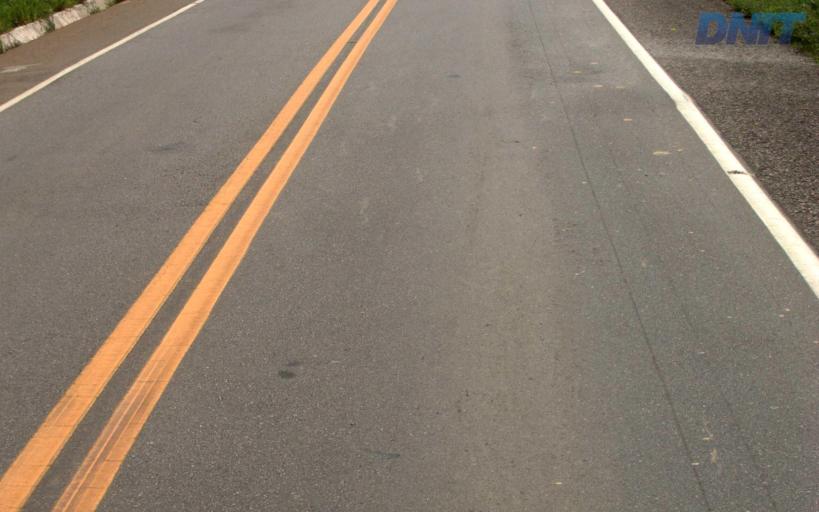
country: BR
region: Minas Gerais
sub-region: Belo Oriente
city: Belo Oriente
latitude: -19.0937
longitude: -42.1936
